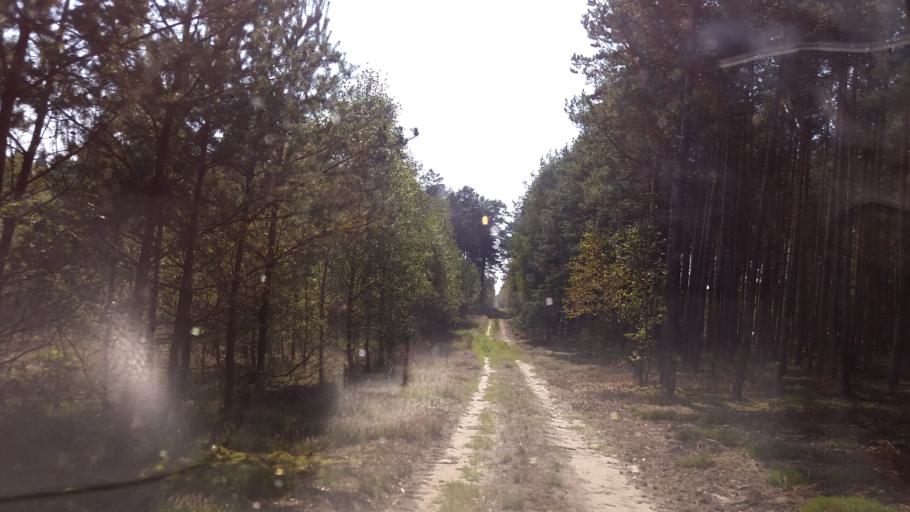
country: PL
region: West Pomeranian Voivodeship
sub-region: Powiat drawski
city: Kalisz Pomorski
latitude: 53.1313
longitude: 15.9404
